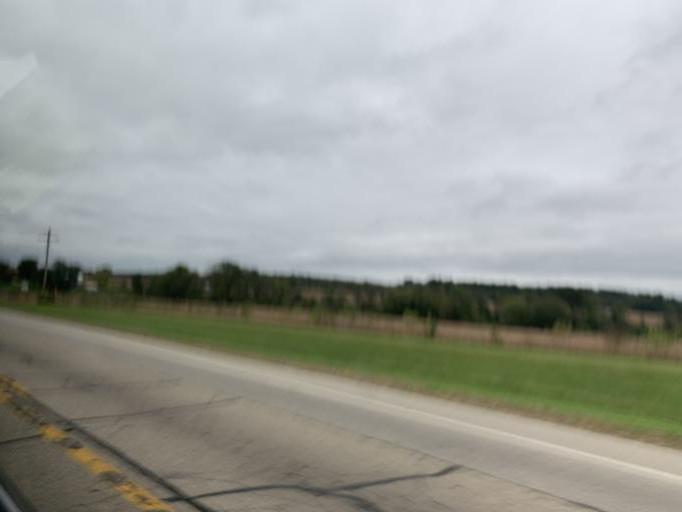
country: US
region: Wisconsin
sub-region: Grant County
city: Muscoda
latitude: 43.2198
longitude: -90.5388
